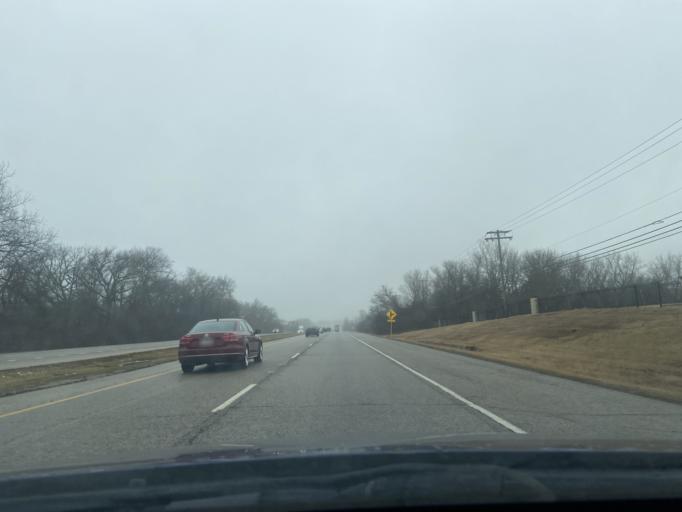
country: US
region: Illinois
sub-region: Lake County
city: Knollwood
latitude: 42.2257
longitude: -88.1114
